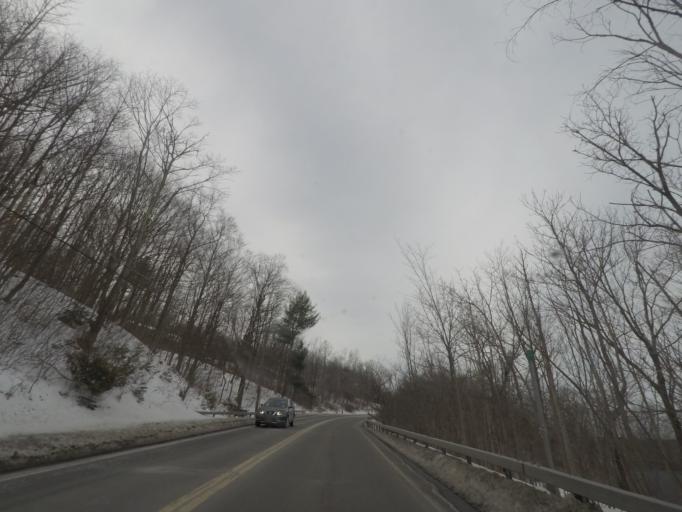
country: US
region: New York
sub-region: Albany County
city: Altamont
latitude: 42.7014
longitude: -74.0357
